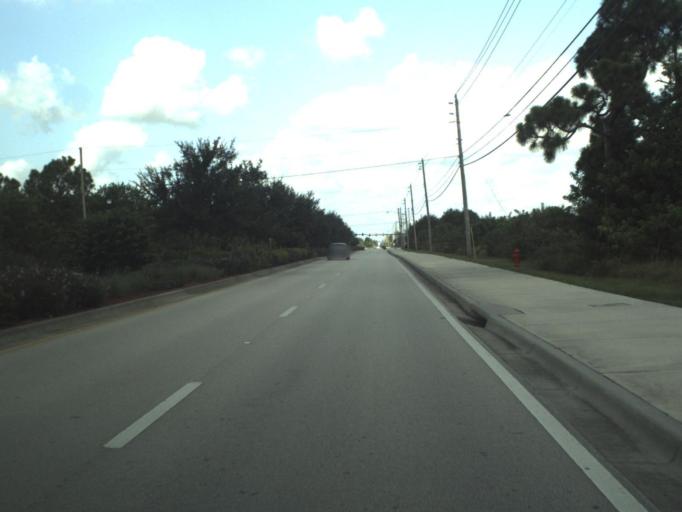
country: US
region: Florida
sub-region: Saint Lucie County
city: Port Saint Lucie
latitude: 27.2097
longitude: -80.3673
